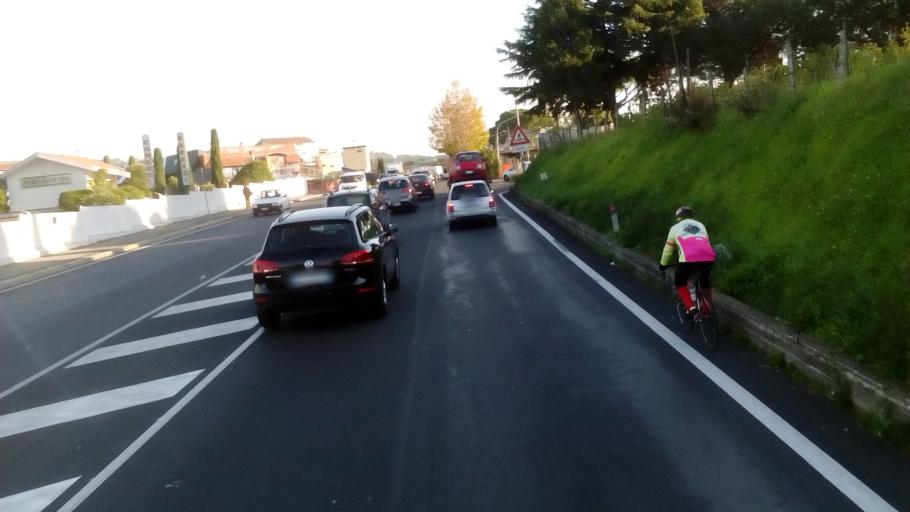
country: IT
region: Latium
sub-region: Citta metropolitana di Roma Capitale
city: Marino
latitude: 41.7686
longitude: 12.6147
